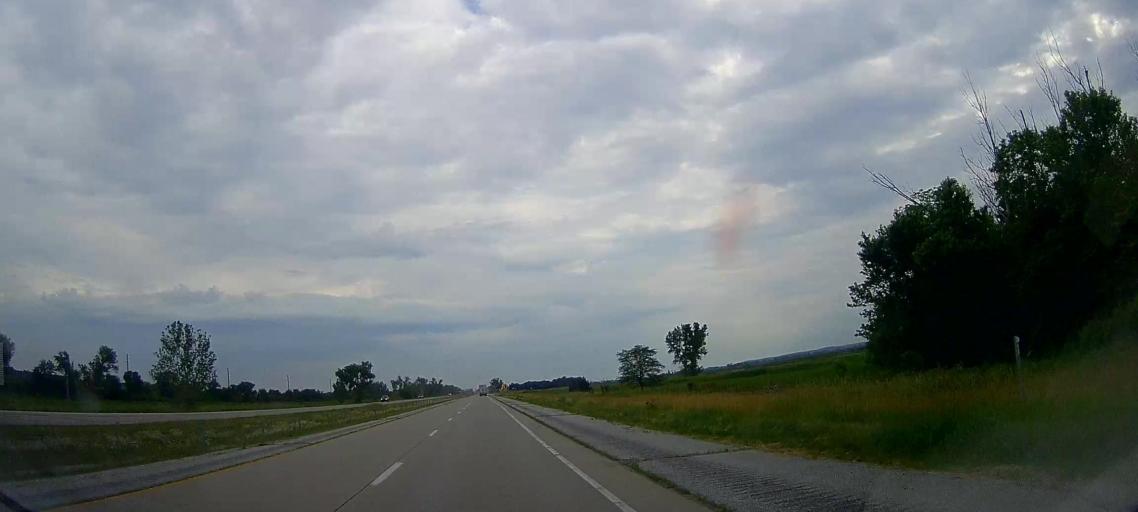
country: US
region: Iowa
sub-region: Harrison County
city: Missouri Valley
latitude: 41.4900
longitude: -95.9009
